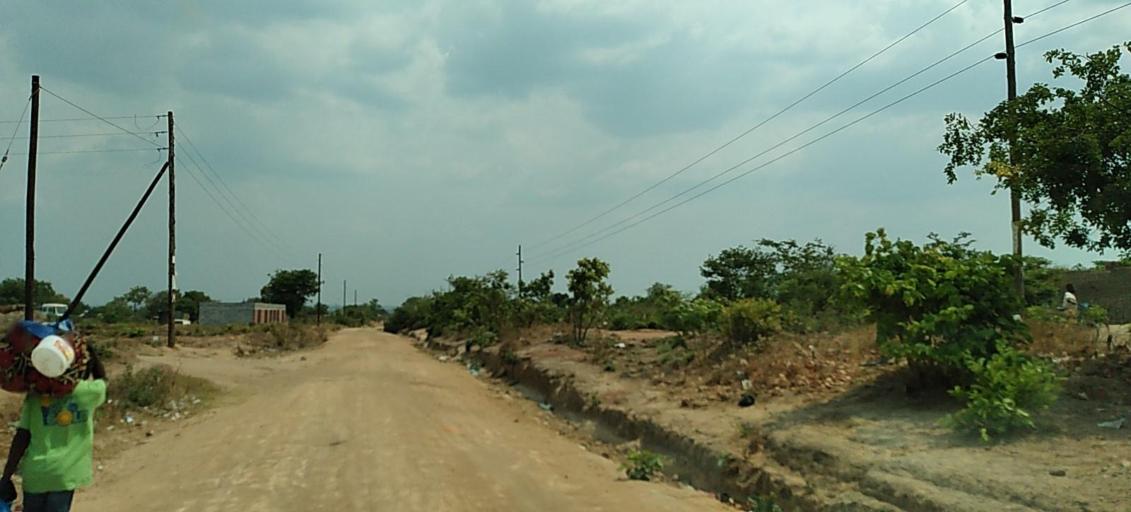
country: ZM
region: Copperbelt
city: Kalulushi
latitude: -12.8609
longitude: 28.0782
